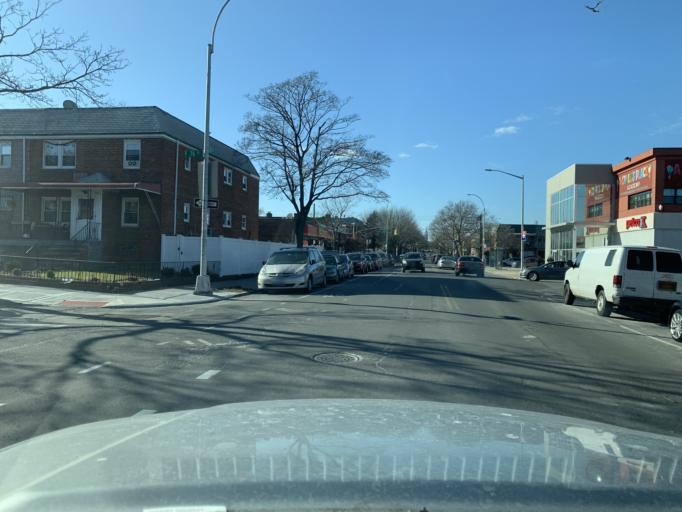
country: US
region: New York
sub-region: Queens County
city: Long Island City
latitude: 40.7587
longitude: -73.8915
